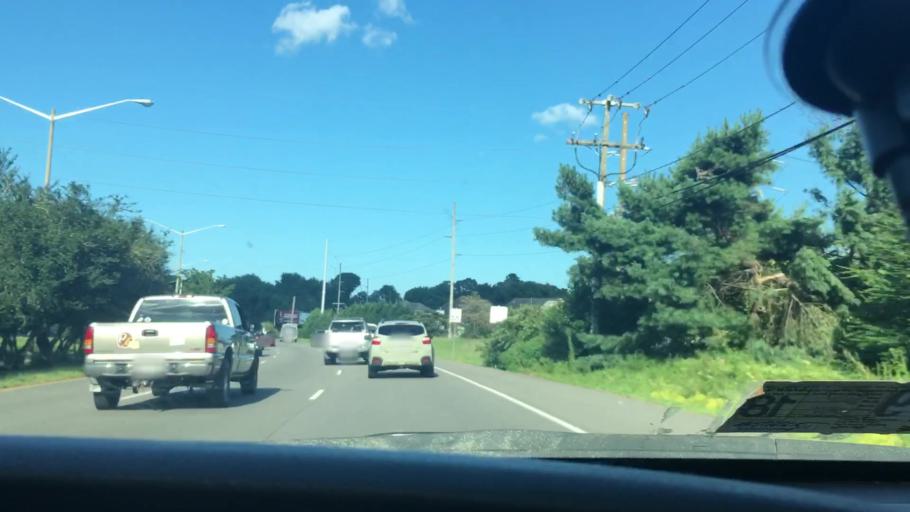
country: US
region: Virginia
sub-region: City of Norfolk
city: Norfolk
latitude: 36.8999
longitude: -76.1329
